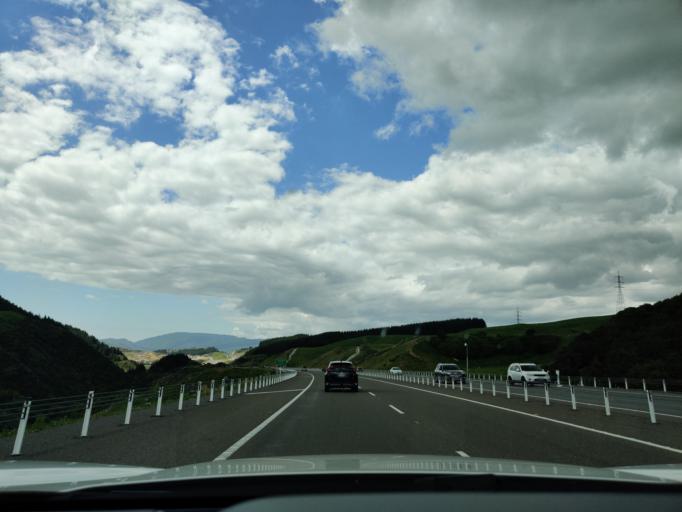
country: NZ
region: Wellington
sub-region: Porirua City
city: Porirua
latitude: -41.1436
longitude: 174.8912
